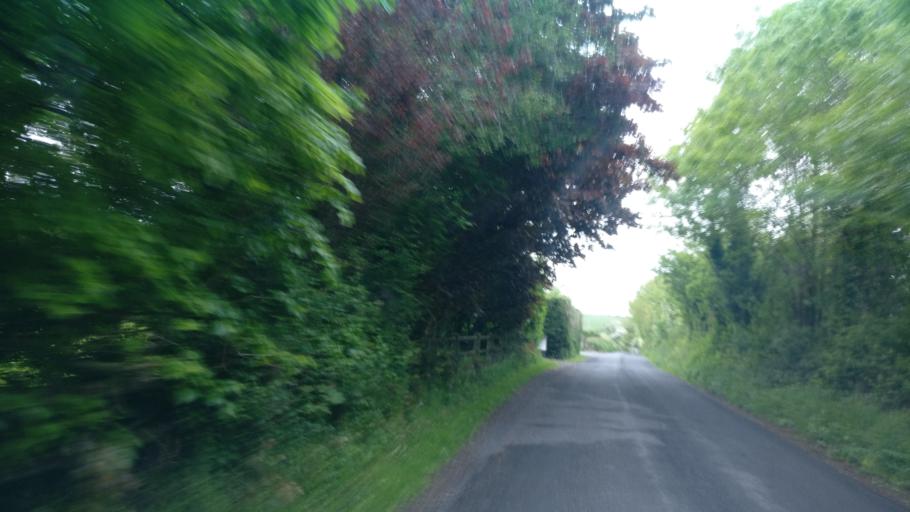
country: IE
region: Connaught
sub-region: County Galway
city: Portumna
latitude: 53.1228
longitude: -8.2910
